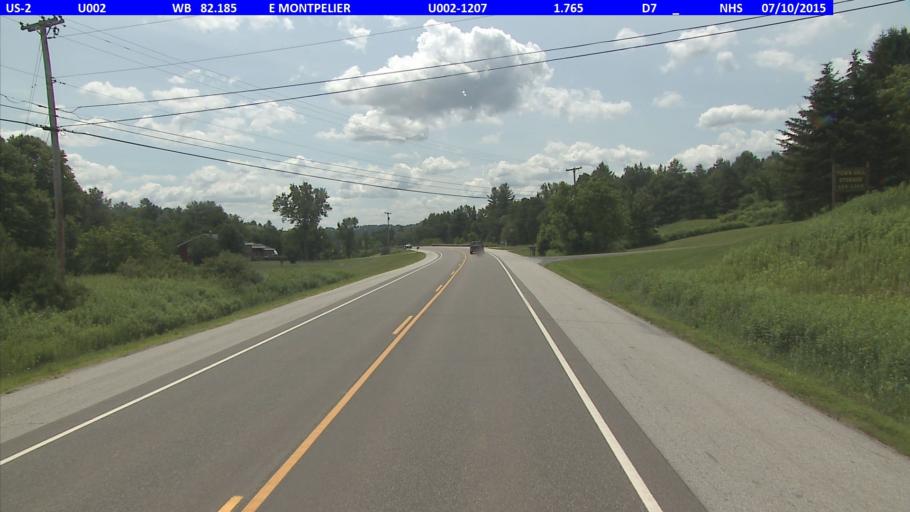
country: US
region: Vermont
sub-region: Washington County
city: Barre
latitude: 44.2583
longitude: -72.5015
